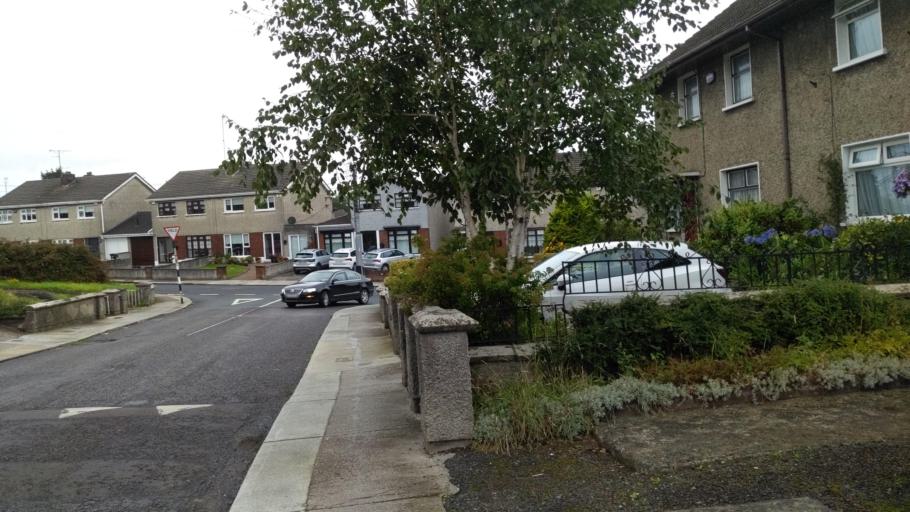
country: IE
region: Leinster
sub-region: Lu
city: Drogheda
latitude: 53.7090
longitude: -6.3585
